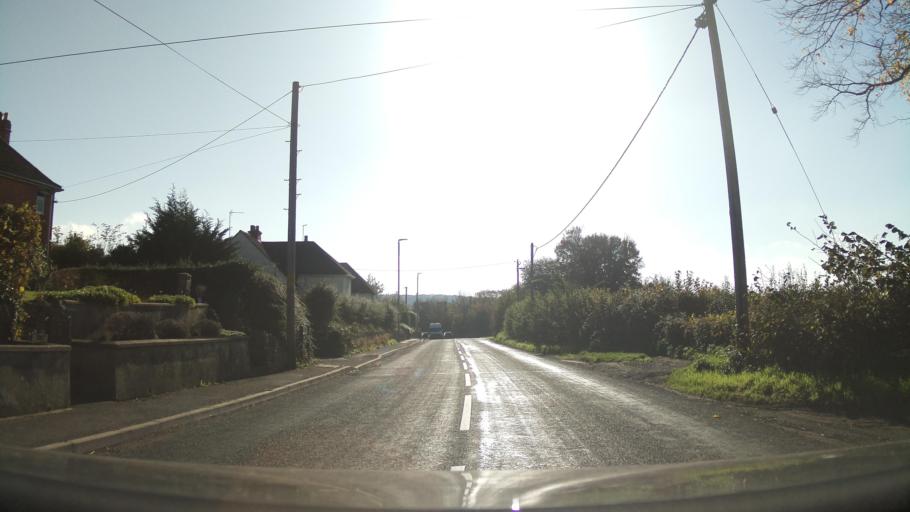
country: GB
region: England
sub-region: Somerset
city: Bruton
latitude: 51.1182
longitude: -2.4494
